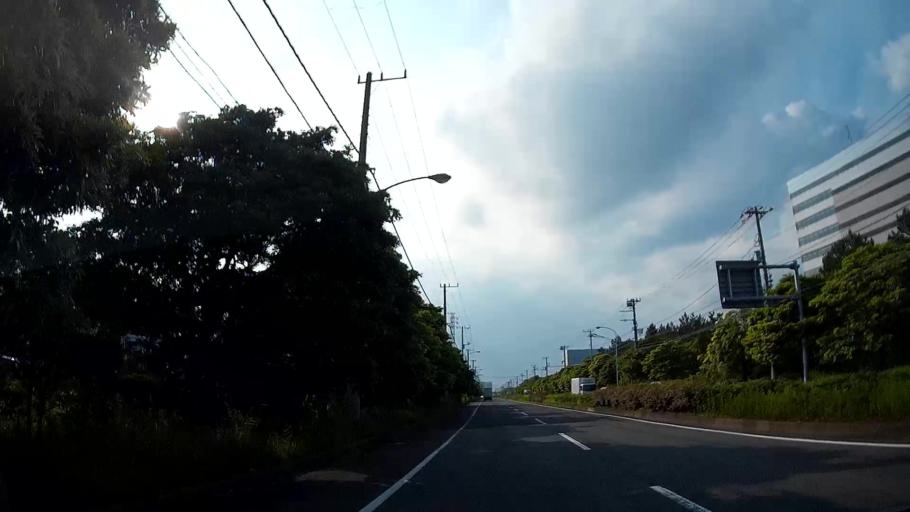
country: JP
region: Chiba
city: Funabashi
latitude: 35.6629
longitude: 140.0106
